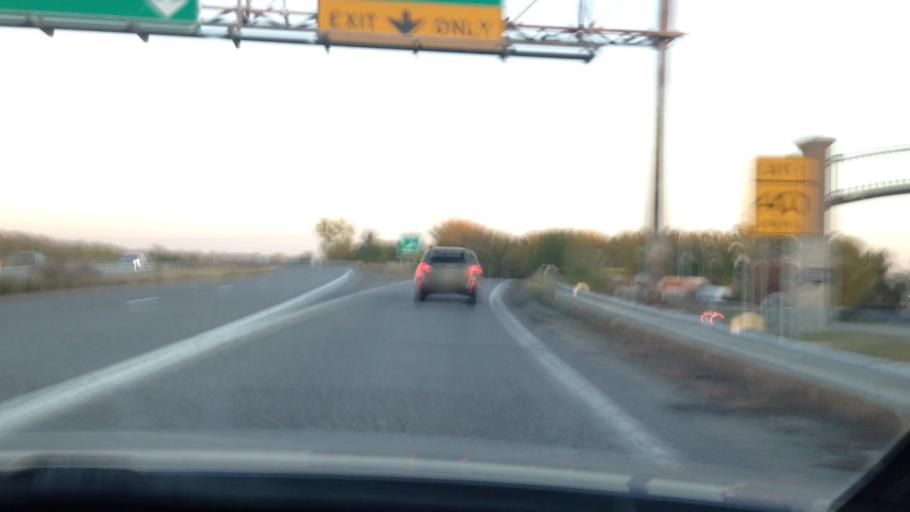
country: US
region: Missouri
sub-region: Platte County
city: Riverside
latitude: 39.1676
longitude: -94.6160
